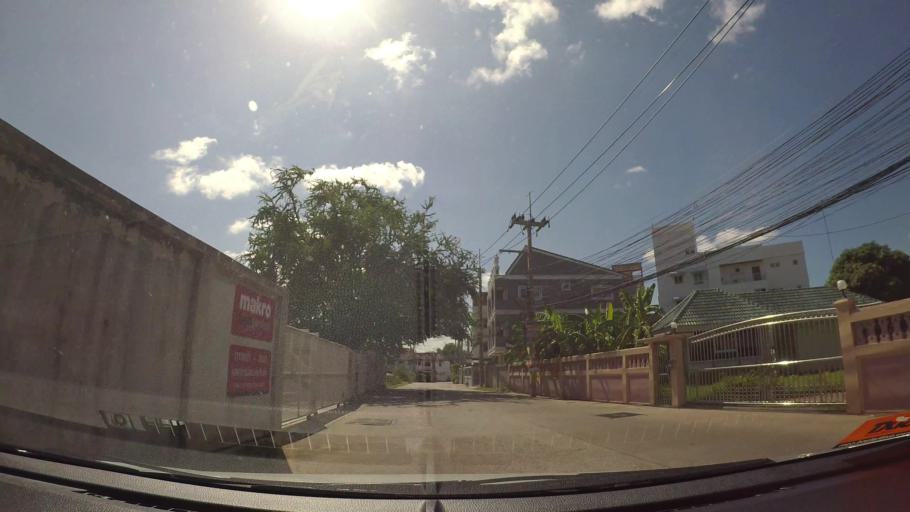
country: TH
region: Chon Buri
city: Phatthaya
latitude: 12.9479
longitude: 100.9028
